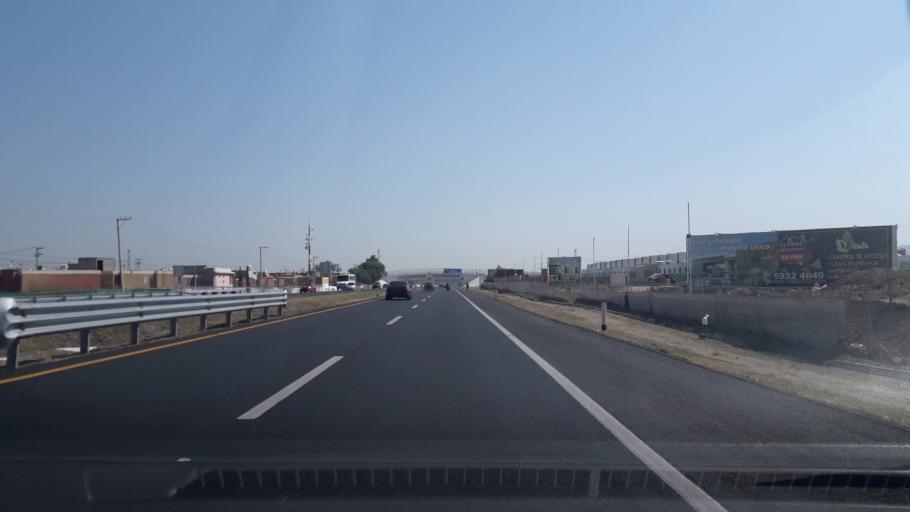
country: MX
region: Mexico
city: Santo Tomas Chiconautla
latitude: 19.6258
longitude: -99.0258
